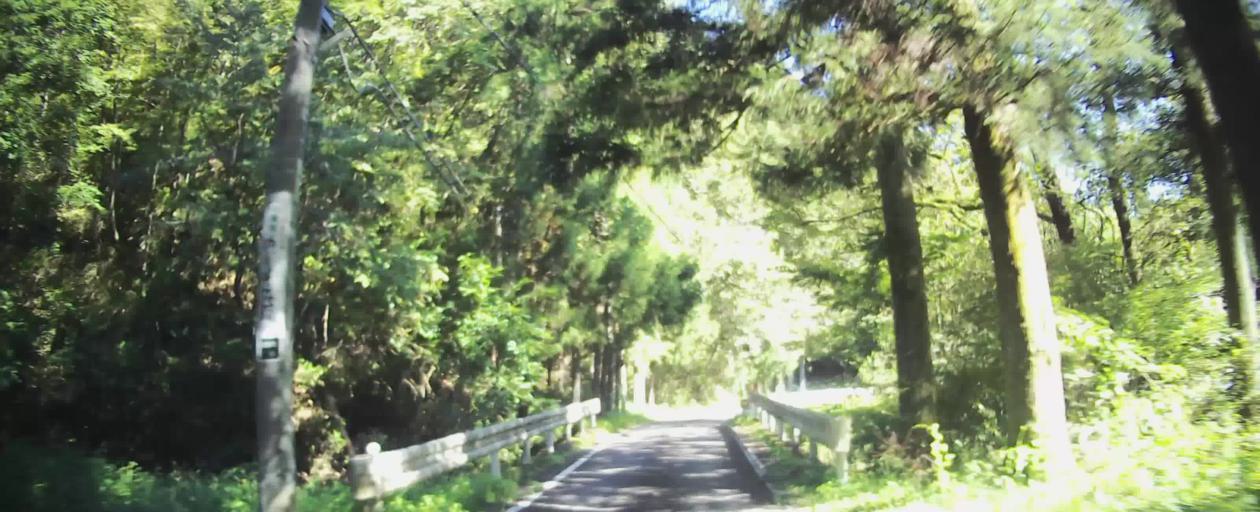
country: JP
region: Gunma
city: Nakanojomachi
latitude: 36.5783
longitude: 138.7294
